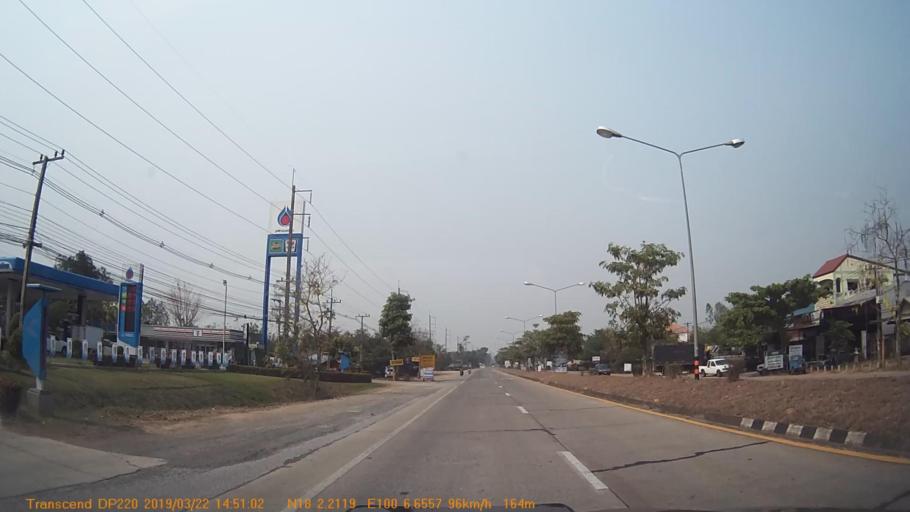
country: TH
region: Phrae
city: Sung Men
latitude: 18.0372
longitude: 100.1110
